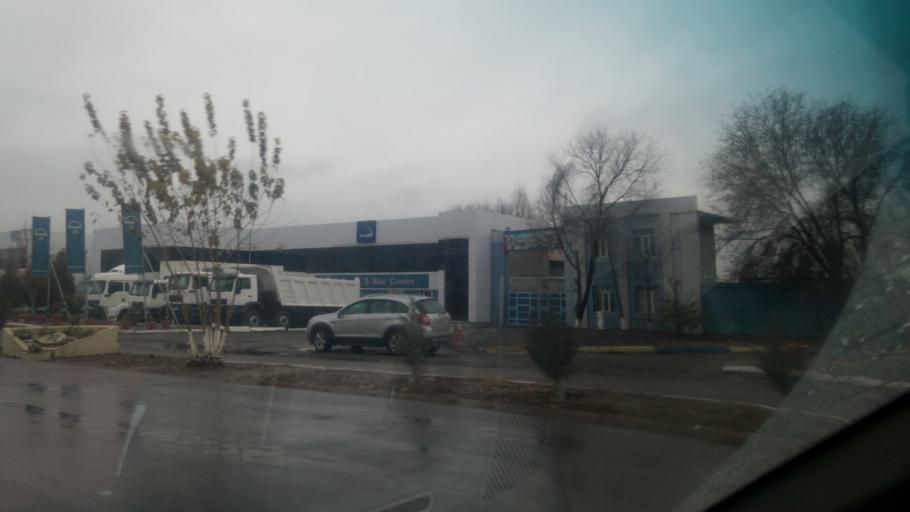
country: UZ
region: Toshkent
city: Urtaowul
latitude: 41.2332
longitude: 69.1574
